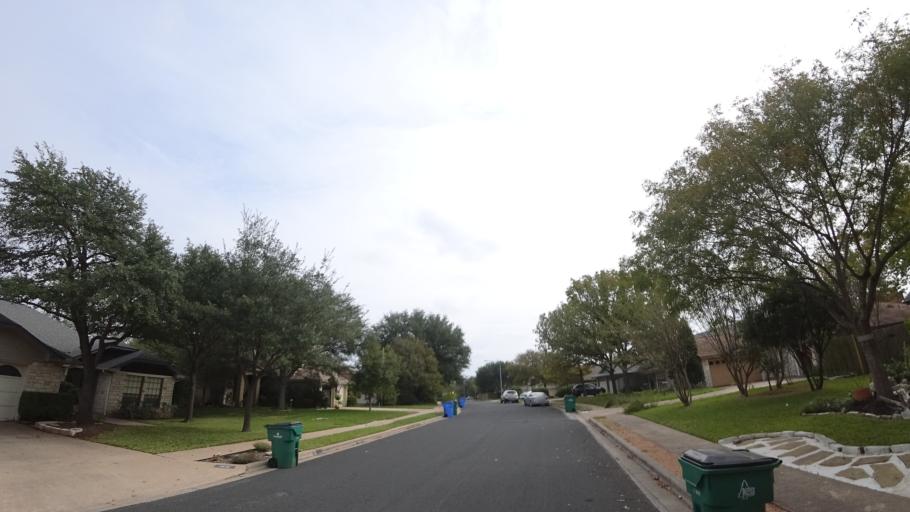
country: US
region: Texas
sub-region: Travis County
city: Wells Branch
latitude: 30.4387
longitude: -97.6788
